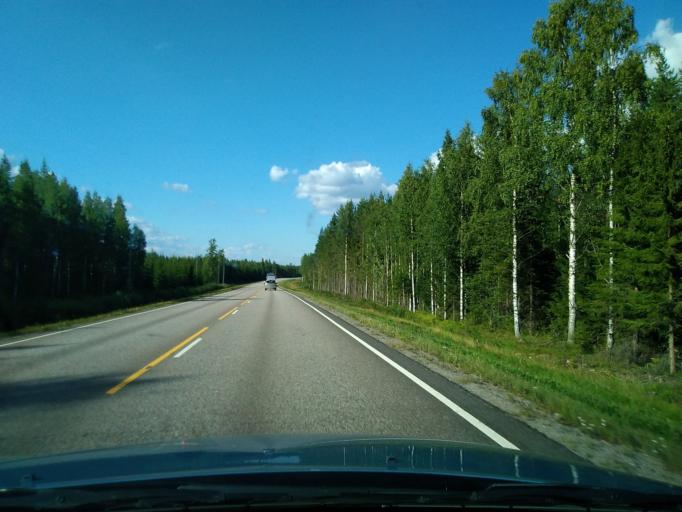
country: FI
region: Pirkanmaa
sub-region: Ylae-Pirkanmaa
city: Maenttae
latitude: 62.0611
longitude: 24.7203
